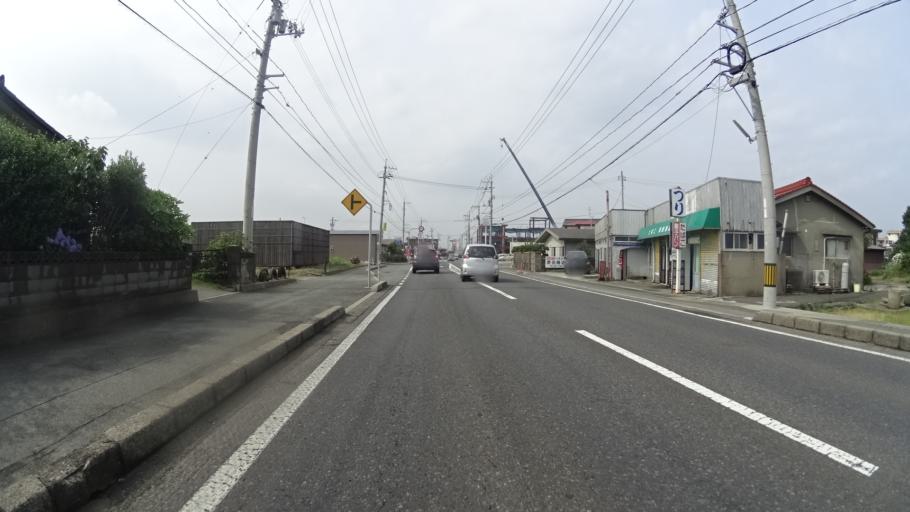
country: JP
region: Yamaguchi
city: Shimonoseki
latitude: 34.0361
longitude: 130.9136
